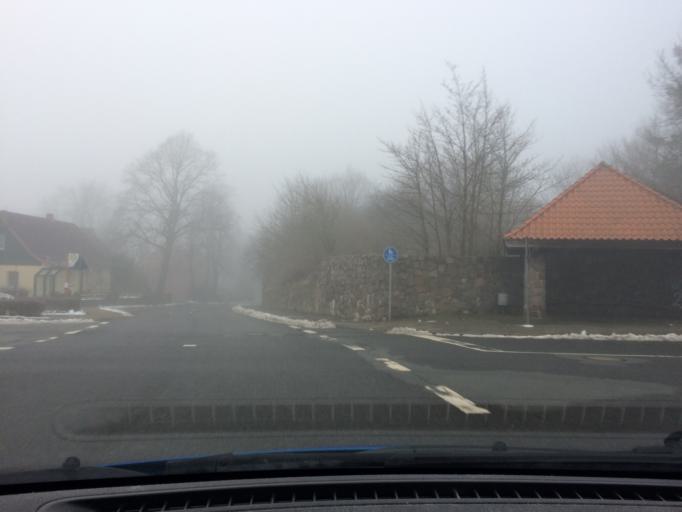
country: DE
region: Schleswig-Holstein
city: Gulzow
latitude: 53.4421
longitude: 10.4909
